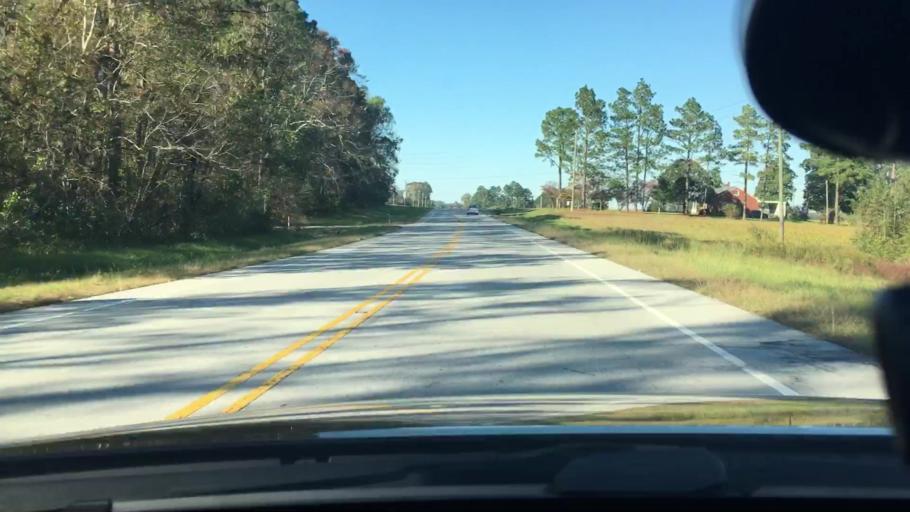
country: US
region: North Carolina
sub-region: Craven County
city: Trent Woods
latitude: 35.1801
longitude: -77.1314
